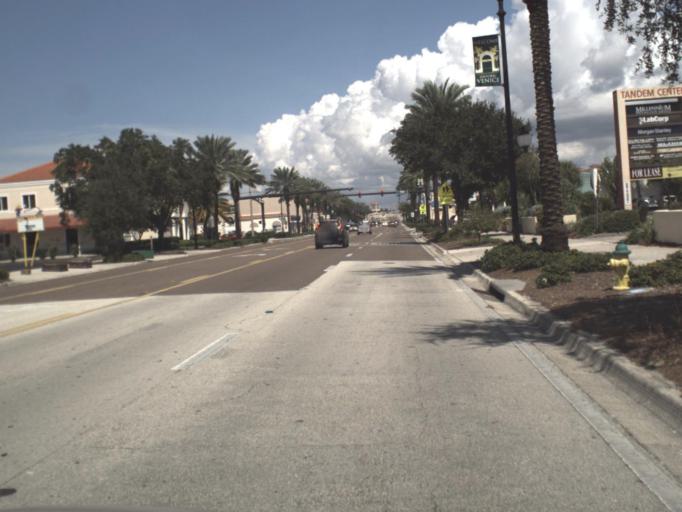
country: US
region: Florida
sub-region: Sarasota County
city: Venice
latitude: 27.0948
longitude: -82.4443
